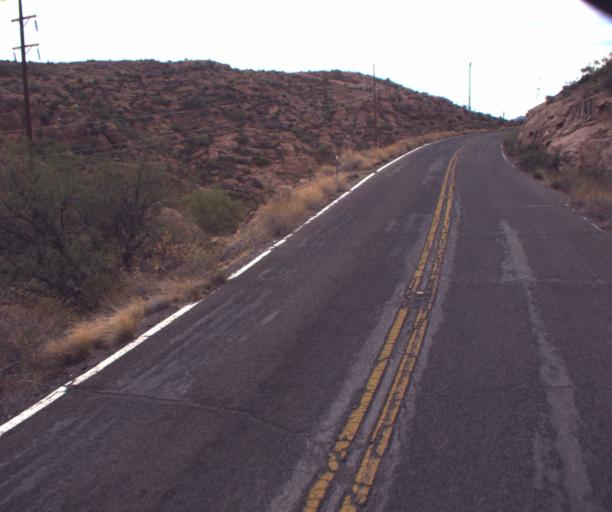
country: US
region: Arizona
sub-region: Pinal County
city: Apache Junction
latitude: 33.5297
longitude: -111.4051
